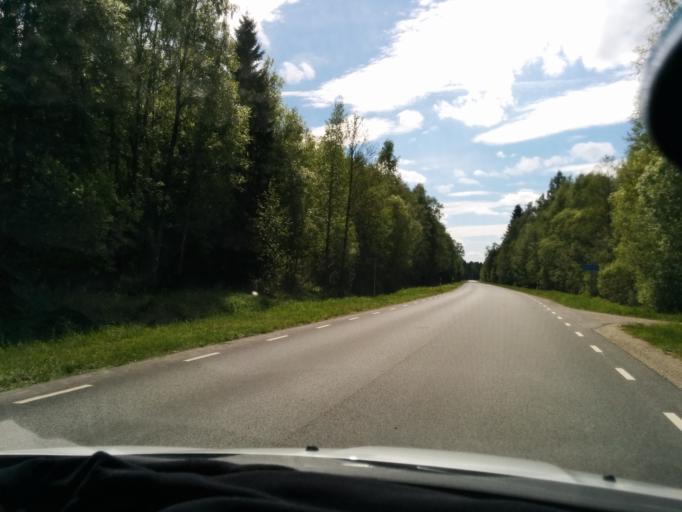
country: EE
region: Harju
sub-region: Loksa linn
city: Loksa
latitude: 59.5500
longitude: 25.7747
